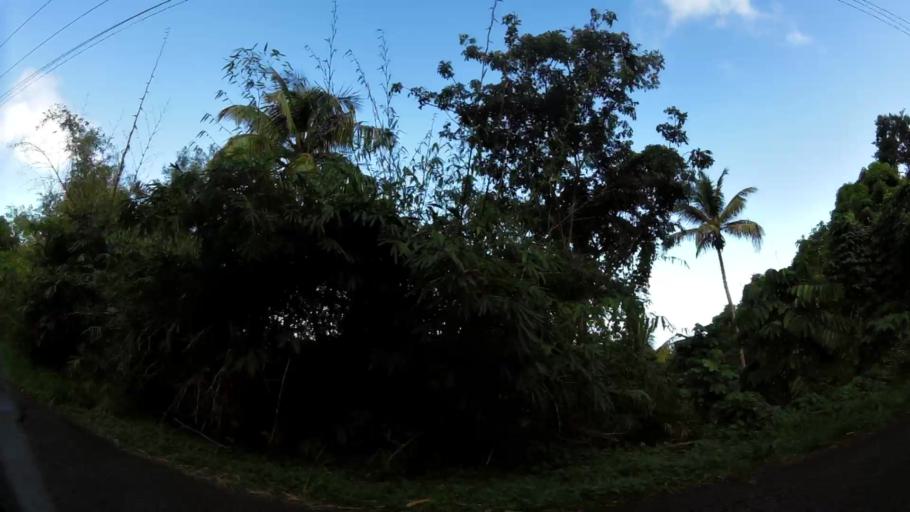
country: LC
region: Anse-la-Raye
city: Canaries
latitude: 13.9170
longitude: -61.0432
